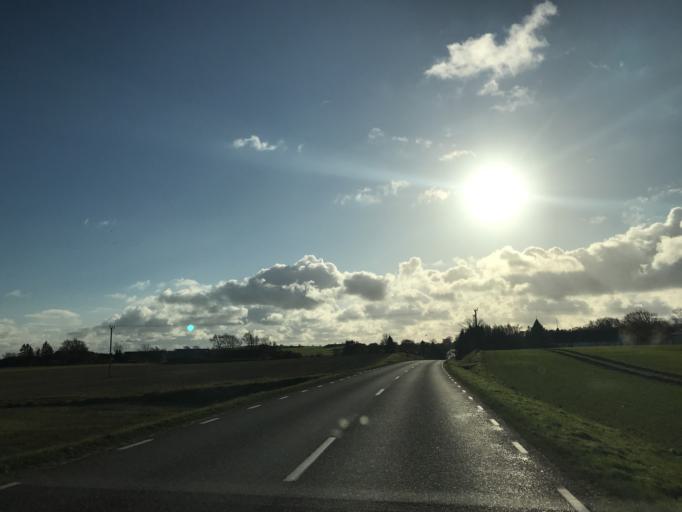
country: SE
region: Skane
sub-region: Skurups Kommun
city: Skurup
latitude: 55.4308
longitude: 13.4726
